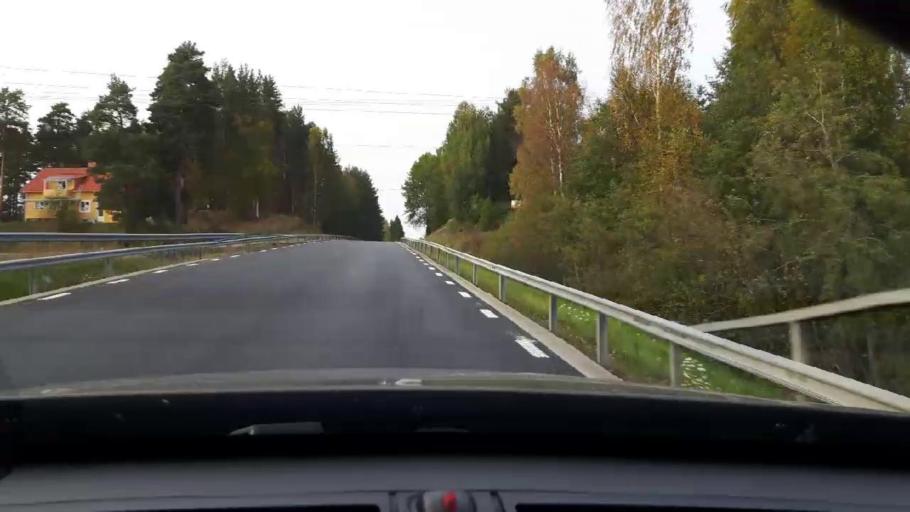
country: SE
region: Dalarna
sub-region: Ludvika Kommun
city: Grangesberg
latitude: 60.2766
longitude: 14.9783
